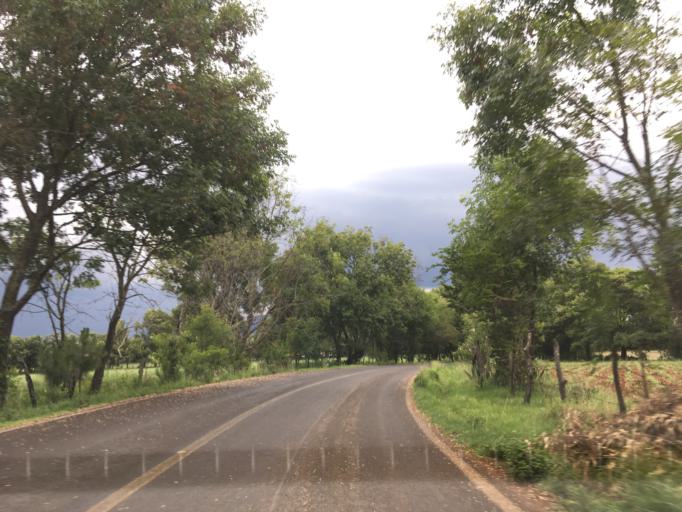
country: MX
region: Michoacan
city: Acuitzio del Canje
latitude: 19.5558
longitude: -101.2700
